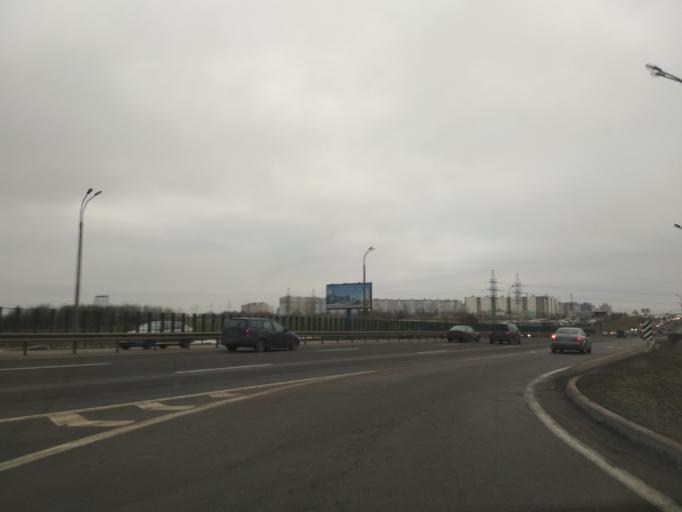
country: BY
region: Minsk
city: Malinovka
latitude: 53.8715
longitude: 27.4215
